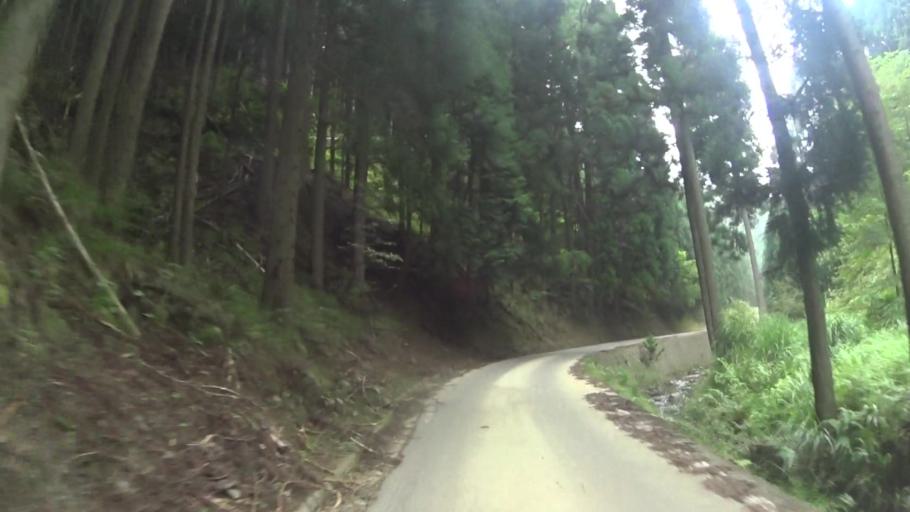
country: JP
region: Kyoto
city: Kameoka
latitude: 35.1641
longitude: 135.5636
